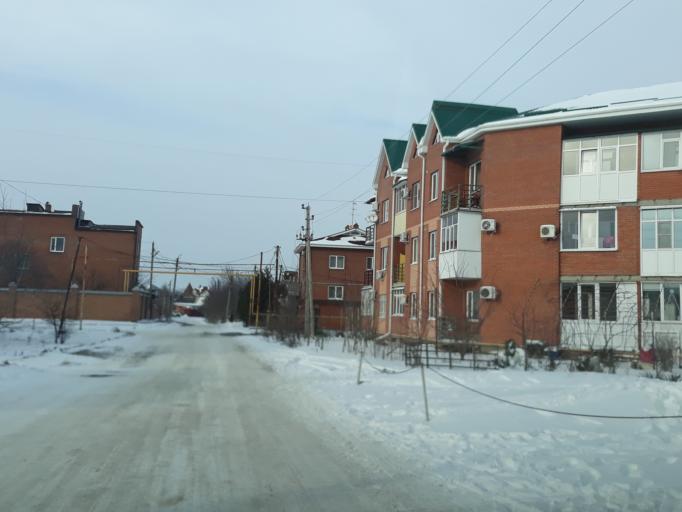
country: RU
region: Rostov
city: Novobessergenovka
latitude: 47.2237
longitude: 38.8422
